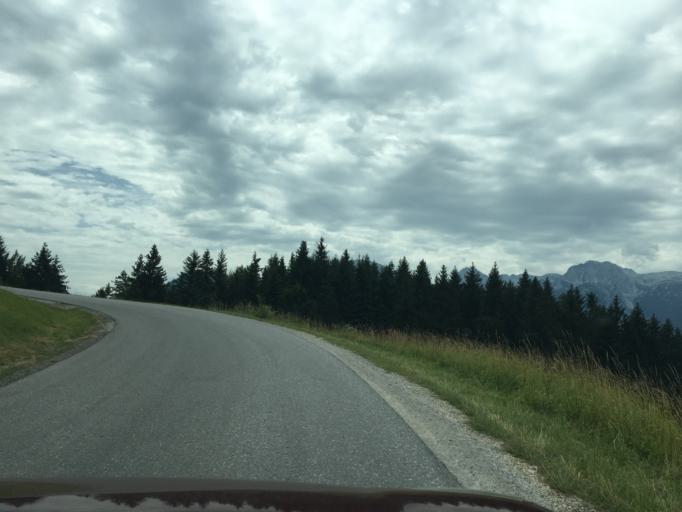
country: AT
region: Salzburg
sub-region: Politischer Bezirk Hallein
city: Abtenau
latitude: 47.6031
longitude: 13.3645
